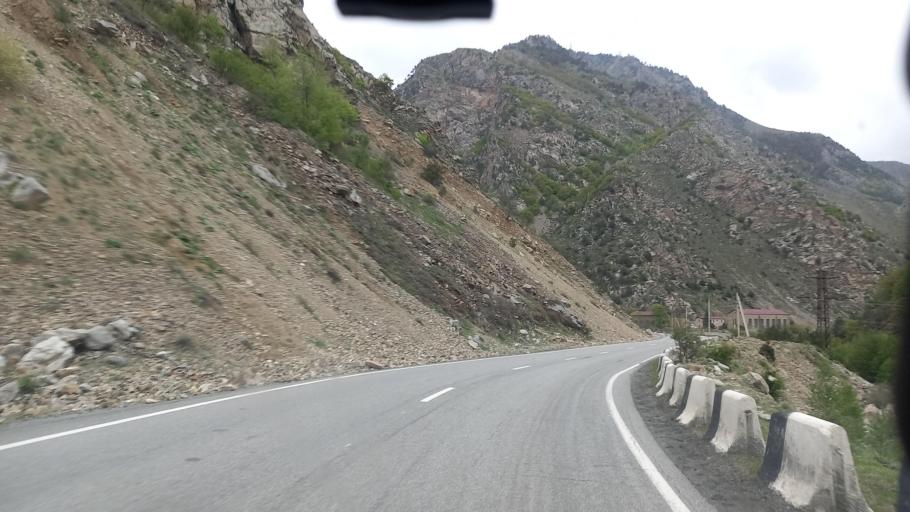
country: RU
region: North Ossetia
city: Mizur
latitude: 42.8360
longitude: 44.0269
